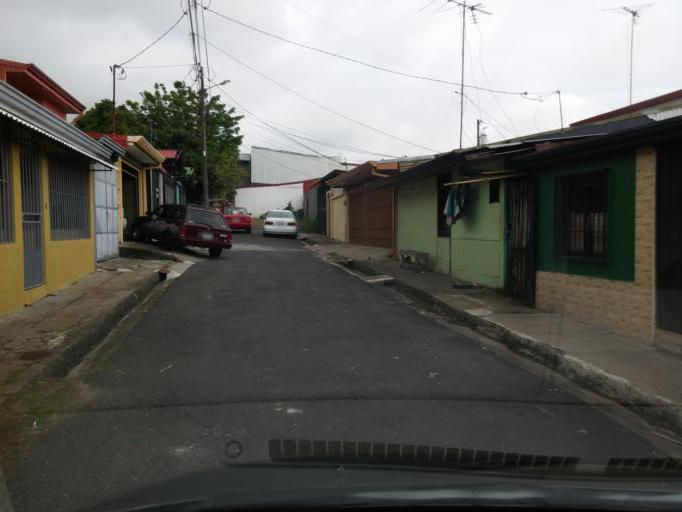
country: CR
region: Heredia
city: Mercedes
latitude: 10.0247
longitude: -84.1290
